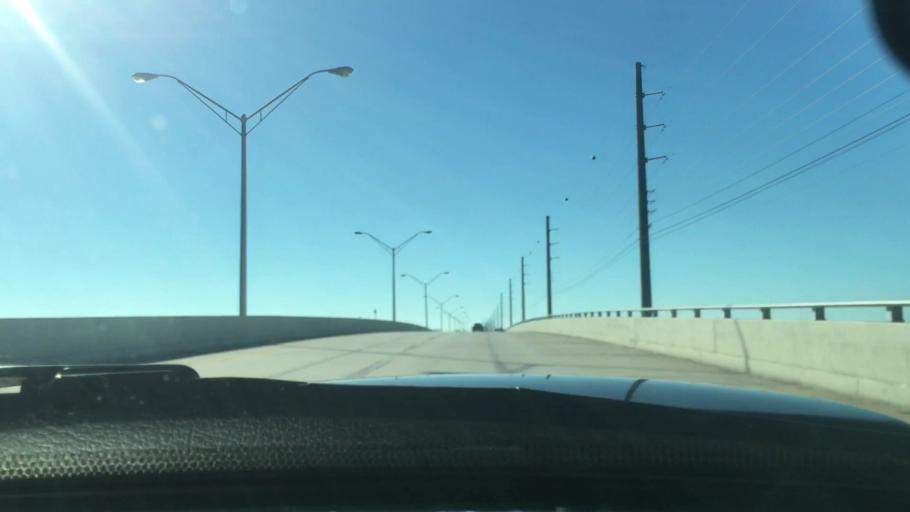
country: US
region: Florida
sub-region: Monroe County
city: Stock Island
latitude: 24.5779
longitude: -81.7156
